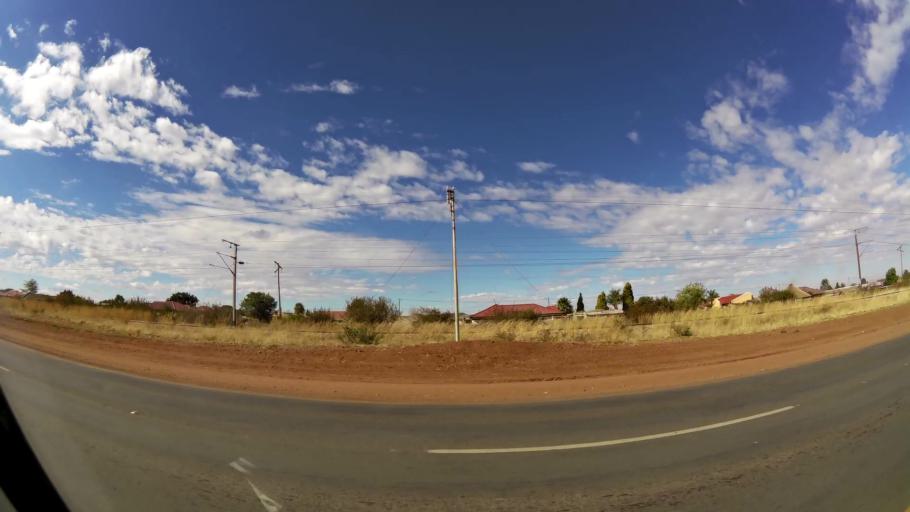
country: ZA
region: Limpopo
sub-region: Waterberg District Municipality
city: Bela-Bela
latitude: -24.8715
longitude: 28.3196
